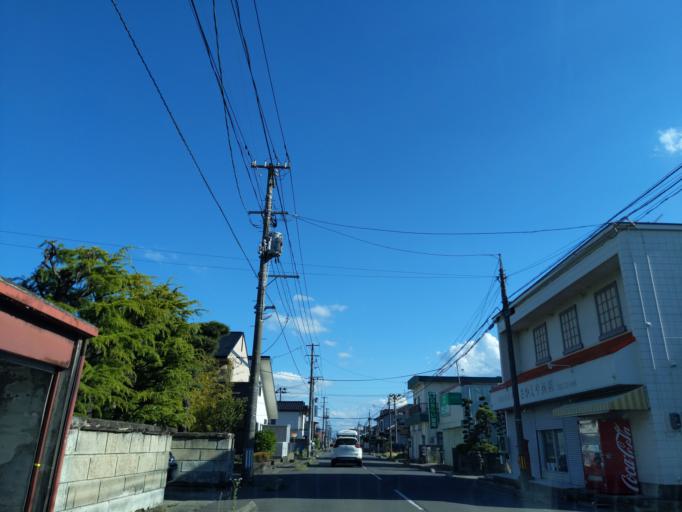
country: JP
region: Fukushima
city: Koriyama
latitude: 37.3899
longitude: 140.3355
